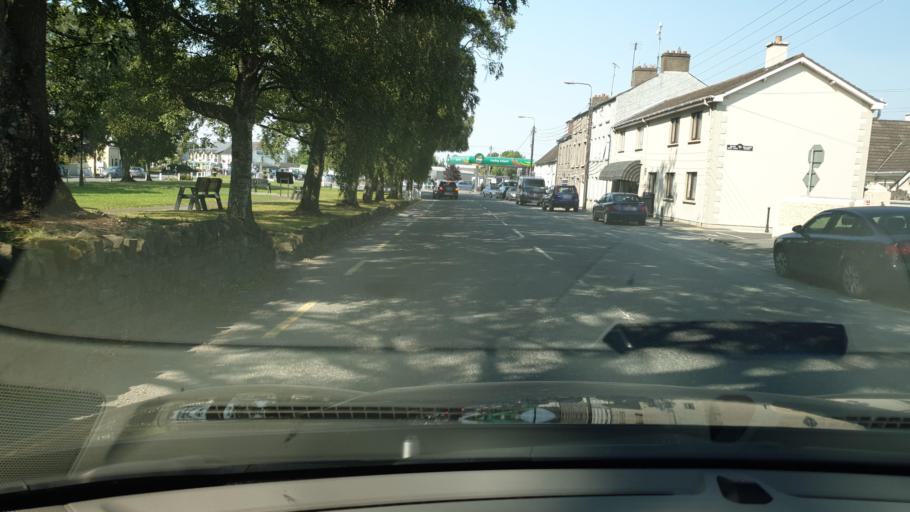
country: IE
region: Leinster
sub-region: An Mhi
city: Newtown Trim
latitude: 53.4805
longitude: -6.7317
